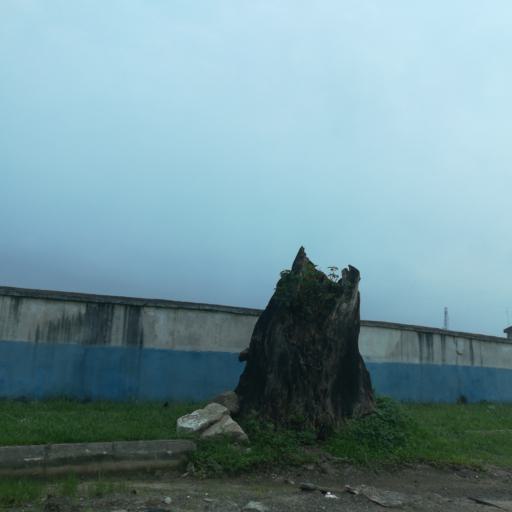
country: NG
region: Rivers
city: Port Harcourt
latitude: 4.7640
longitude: 7.0121
